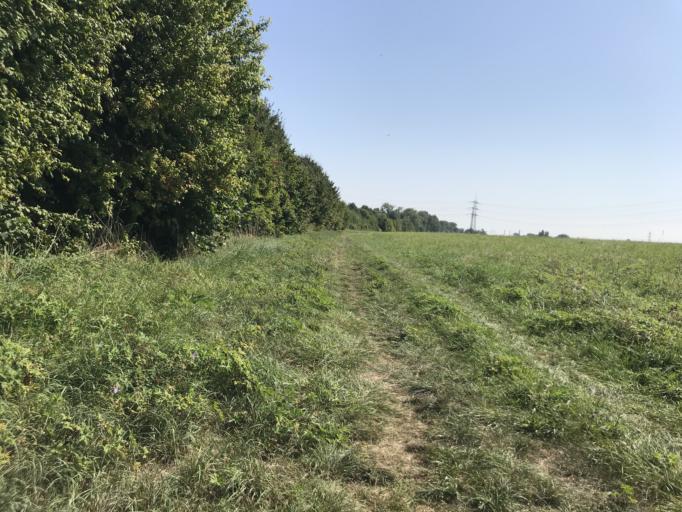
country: DE
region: Hesse
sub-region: Regierungsbezirk Darmstadt
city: Bischofsheim
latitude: 50.0013
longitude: 8.3682
